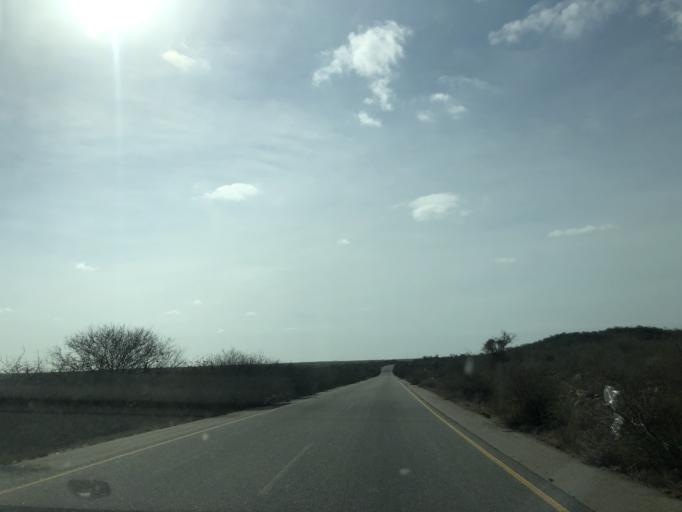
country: AO
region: Benguela
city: Benguela
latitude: -12.8931
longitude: 13.4758
